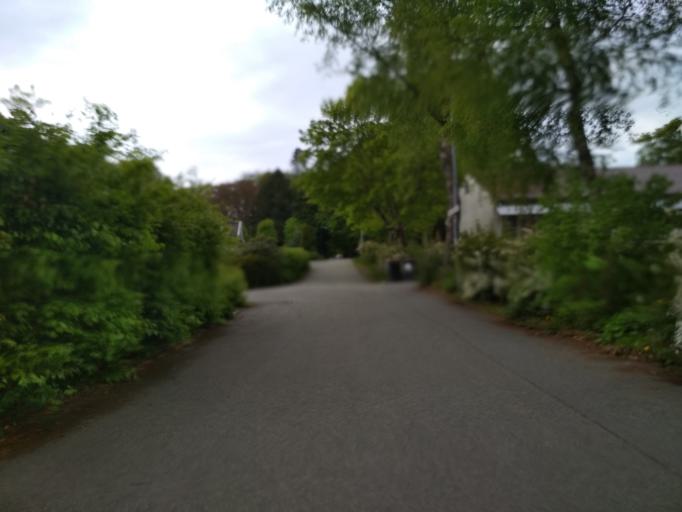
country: NO
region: Rogaland
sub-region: Stavanger
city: Stavanger
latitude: 58.9640
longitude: 5.7219
